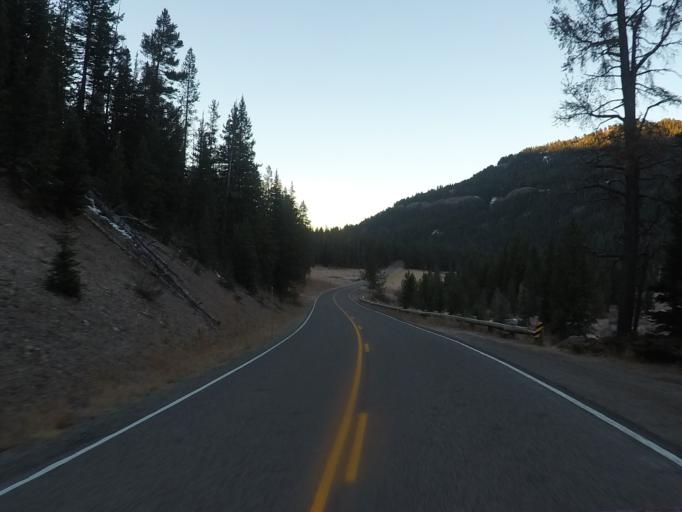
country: US
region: Montana
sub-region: Stillwater County
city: Absarokee
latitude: 44.9536
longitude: -110.0747
